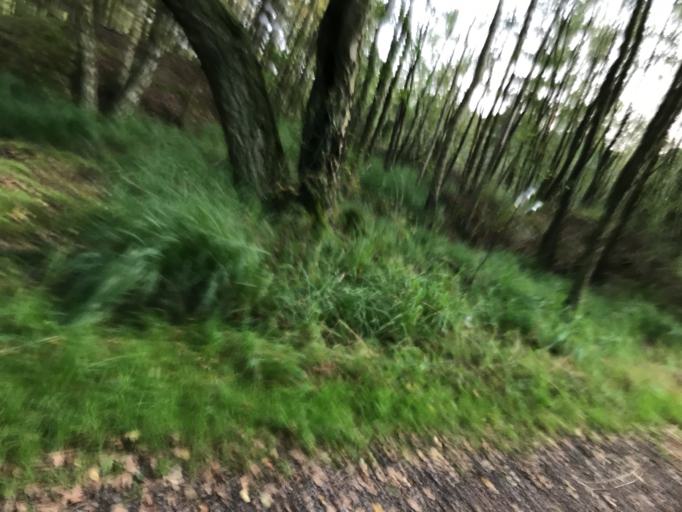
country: SE
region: Vaestra Goetaland
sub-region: Goteborg
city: Majorna
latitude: 57.7290
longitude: 11.8833
